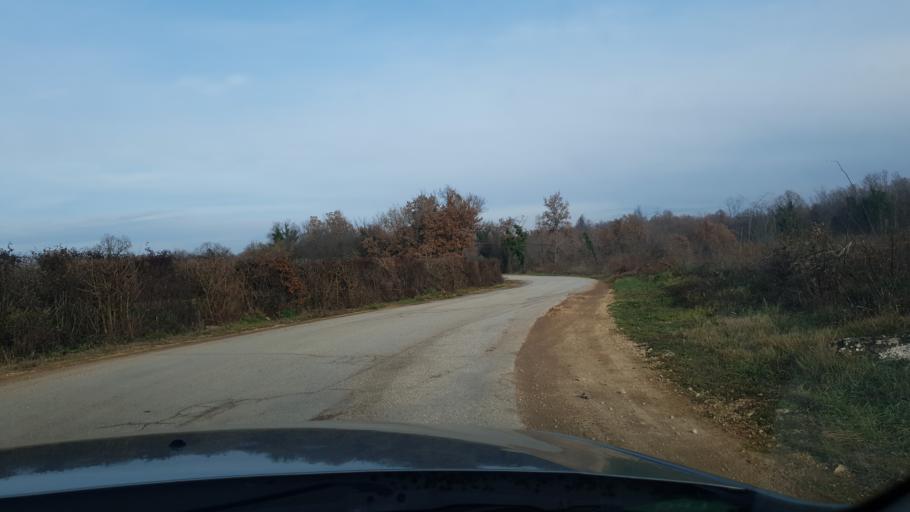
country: HR
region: Istarska
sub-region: Grad Porec
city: Porec
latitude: 45.2356
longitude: 13.6352
